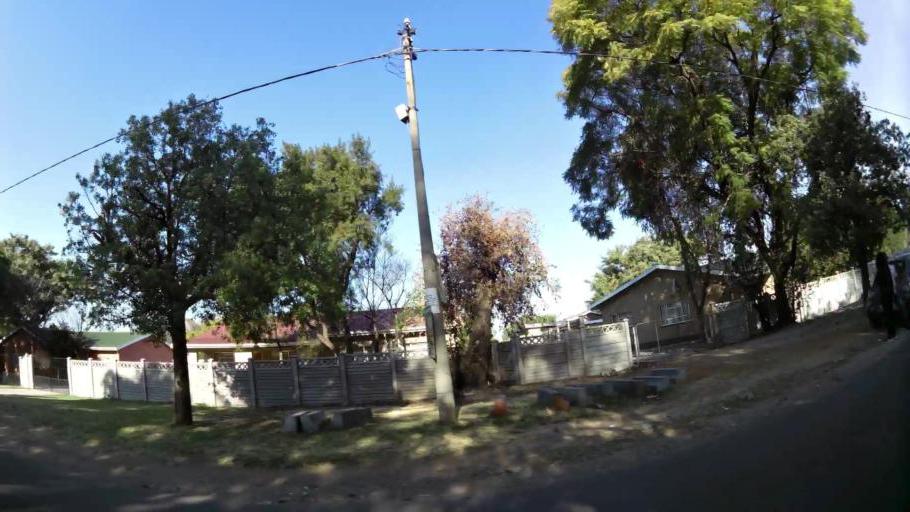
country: ZA
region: North-West
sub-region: Bojanala Platinum District Municipality
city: Rustenburg
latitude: -25.6536
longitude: 27.2381
